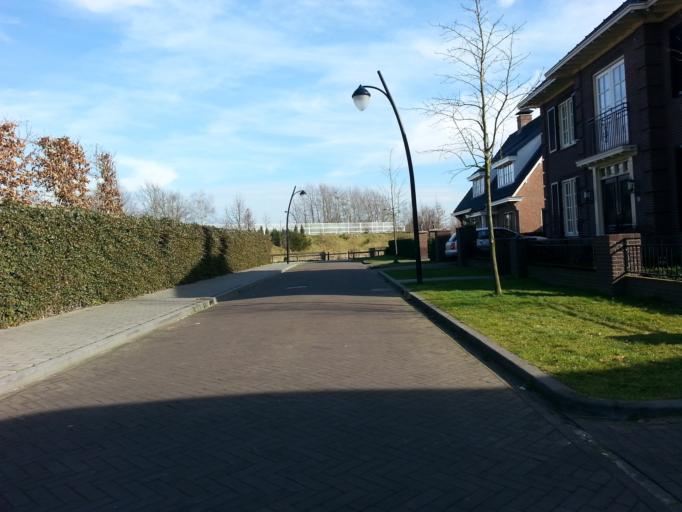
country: NL
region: Utrecht
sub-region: Gemeente Leusden
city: Leusden
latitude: 52.1168
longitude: 5.4155
